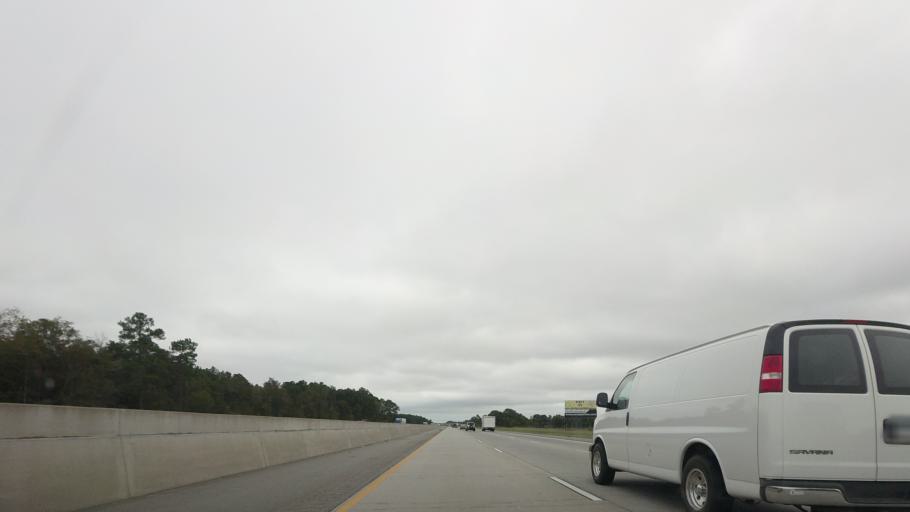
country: US
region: Georgia
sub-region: Tift County
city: Omega
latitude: 31.3066
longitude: -83.4781
